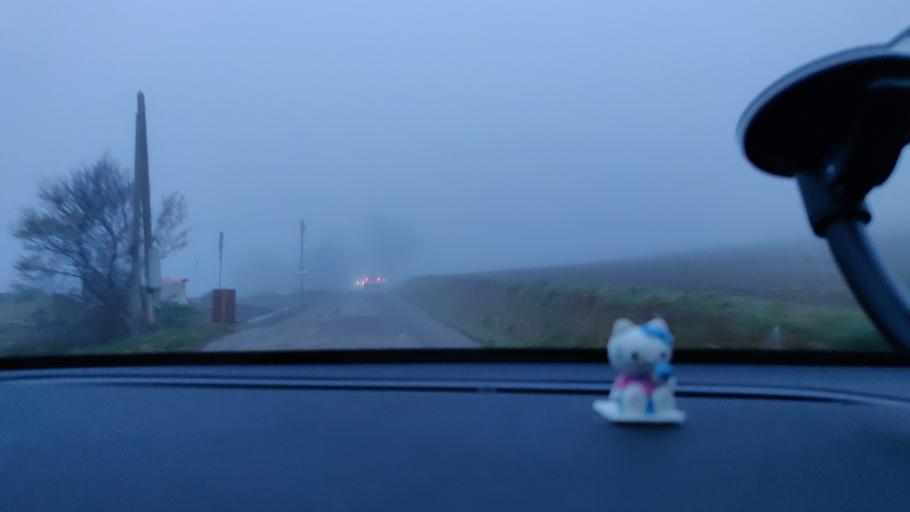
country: FR
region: Midi-Pyrenees
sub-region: Departement de la Haute-Garonne
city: Vieille-Toulouse
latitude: 43.4855
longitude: 1.4547
